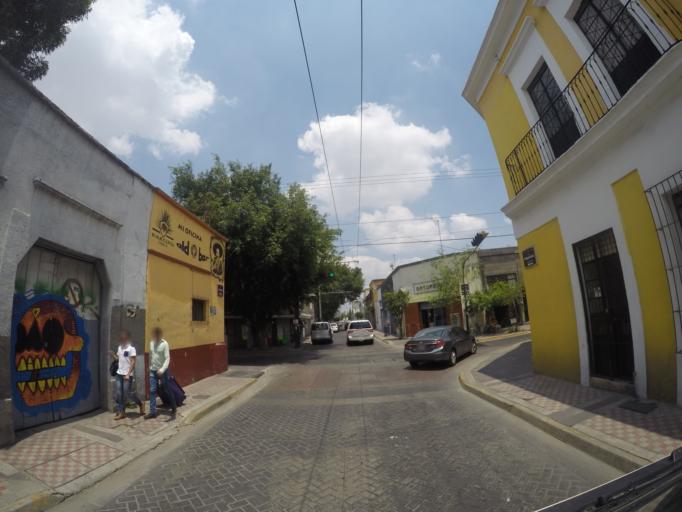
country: MX
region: Jalisco
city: Guadalajara
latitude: 20.6780
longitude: -103.3531
